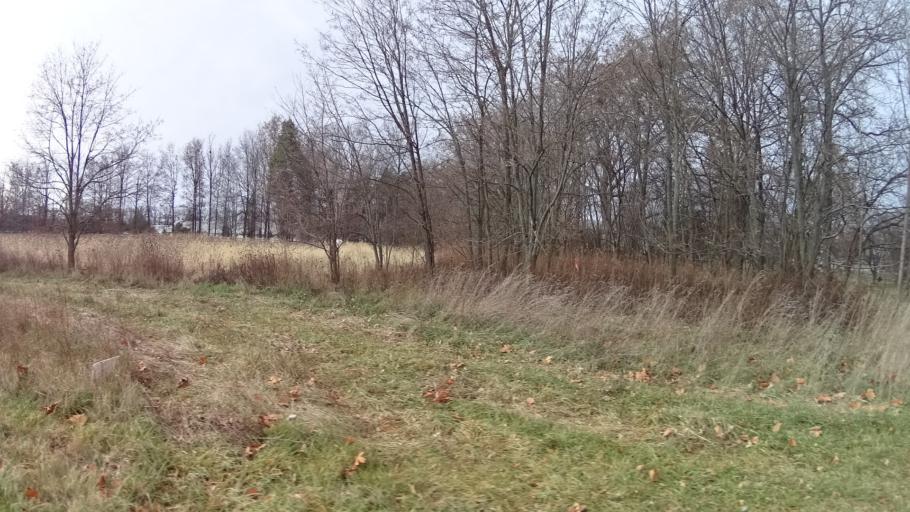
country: US
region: Ohio
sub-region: Lorain County
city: North Ridgeville
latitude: 41.3719
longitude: -82.0368
